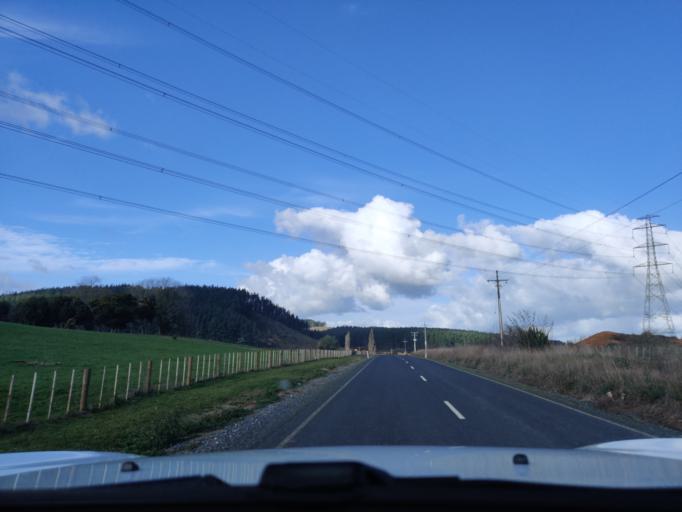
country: NZ
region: Waikato
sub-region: Waikato District
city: Te Kauwhata
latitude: -37.2905
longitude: 175.2212
